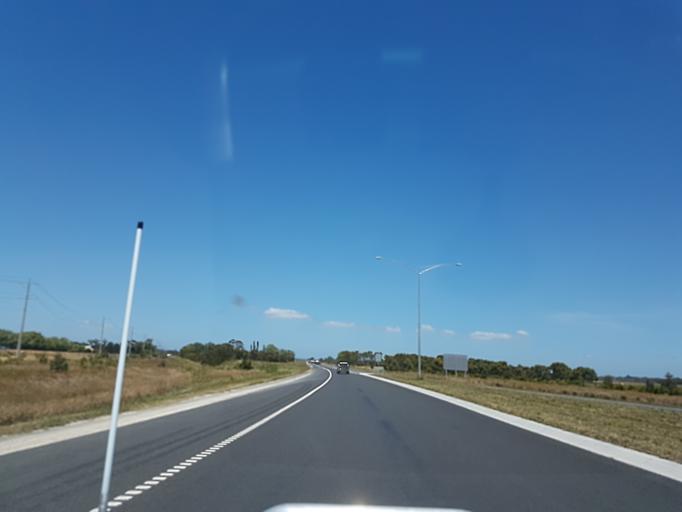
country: AU
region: Victoria
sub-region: Cardinia
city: Koo-Wee-Rup
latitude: -38.1846
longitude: 145.4788
